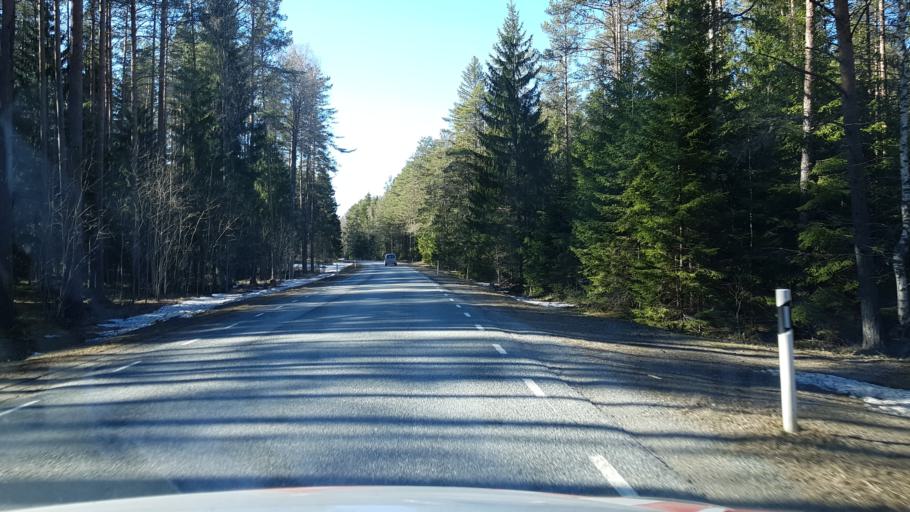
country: EE
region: Laeaene-Virumaa
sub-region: Vinni vald
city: Vinni
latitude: 59.2621
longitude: 26.6800
